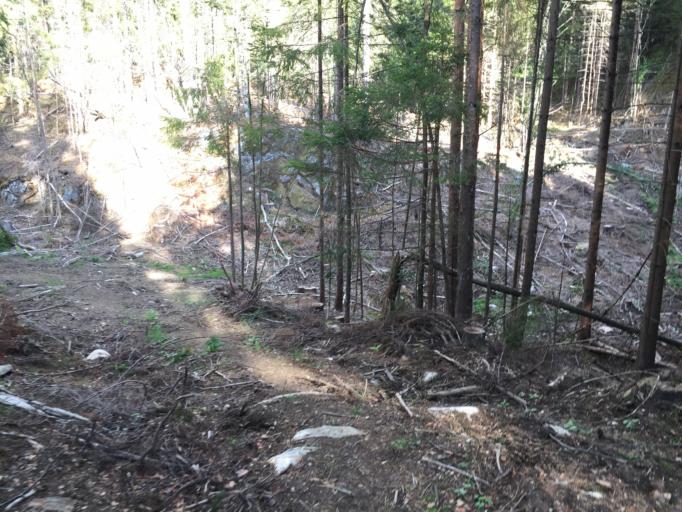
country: NO
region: Akershus
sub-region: Raelingen
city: Fjerdingby
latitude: 59.9194
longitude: 11.0306
